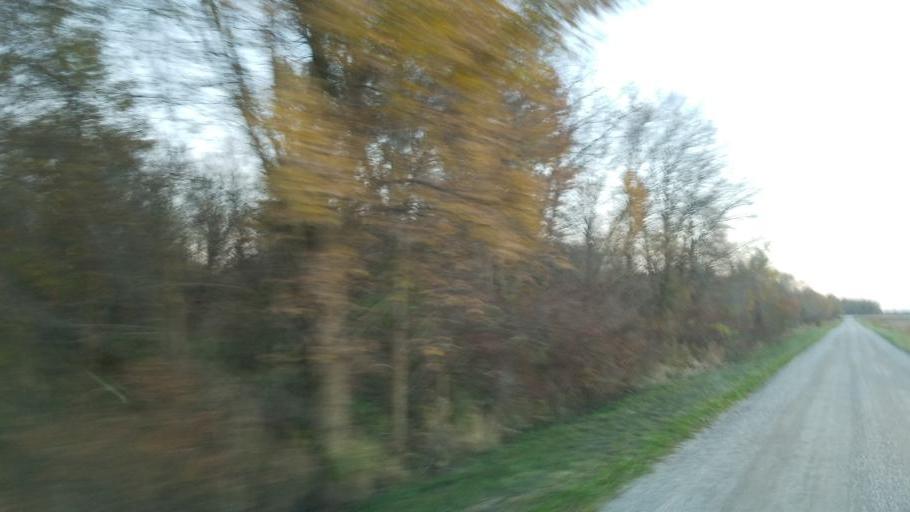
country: US
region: Ohio
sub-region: Huron County
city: Willard
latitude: 41.0032
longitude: -82.7805
